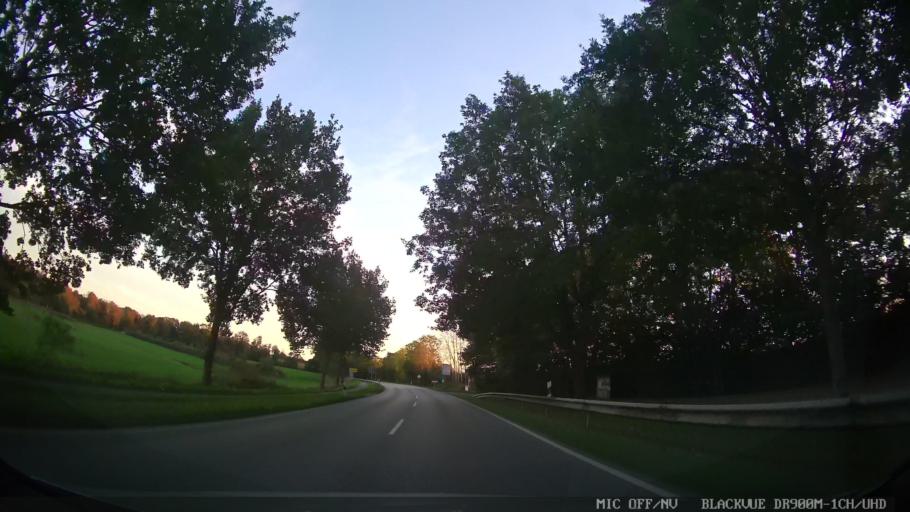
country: DE
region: Schleswig-Holstein
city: Susel
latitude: 54.0739
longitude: 10.6877
